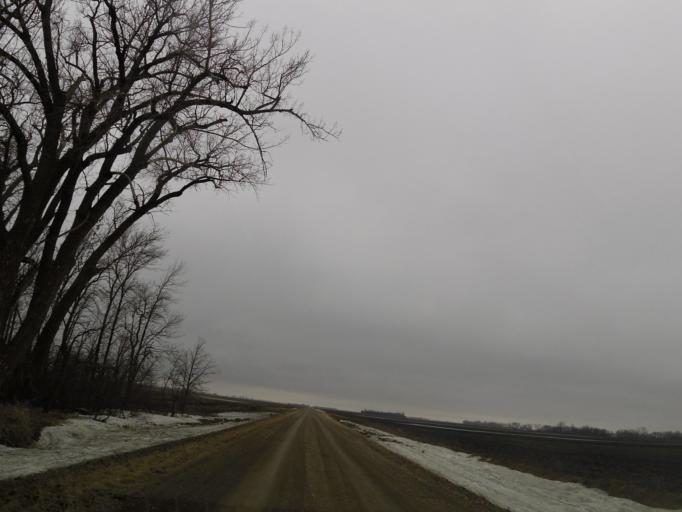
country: US
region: North Dakota
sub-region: Walsh County
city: Grafton
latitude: 48.3831
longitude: -97.1988
